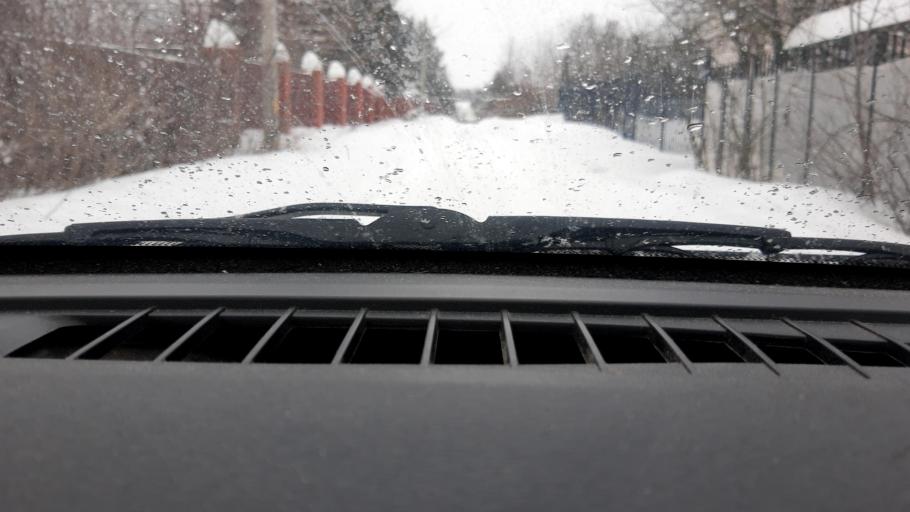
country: RU
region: Moskovskaya
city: Pirogovskiy
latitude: 56.0157
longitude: 37.7255
